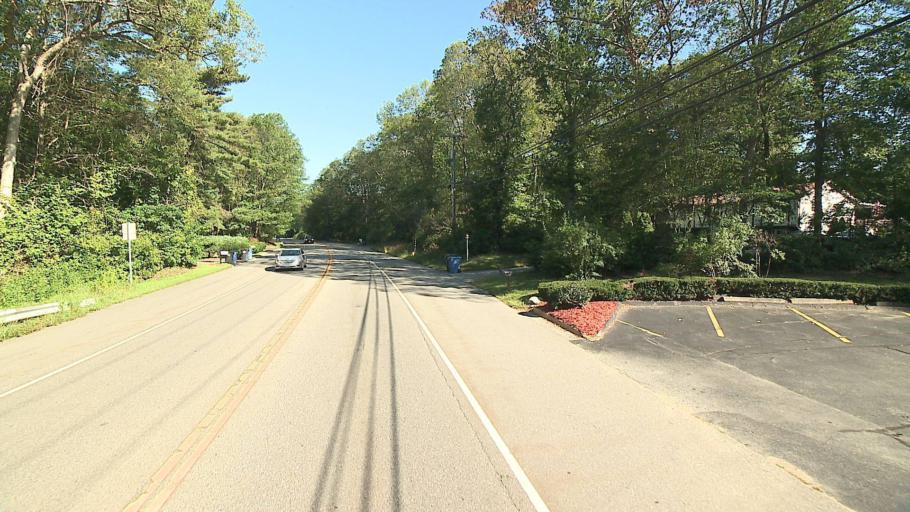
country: US
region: Connecticut
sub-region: New London County
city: Gales Ferry
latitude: 41.4146
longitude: -72.0737
